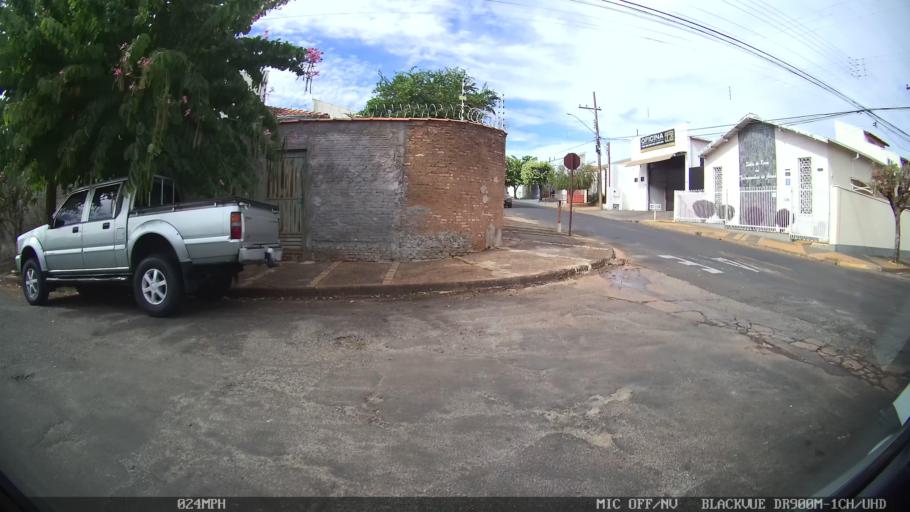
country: BR
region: Sao Paulo
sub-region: Catanduva
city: Catanduva
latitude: -21.1499
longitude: -48.9725
